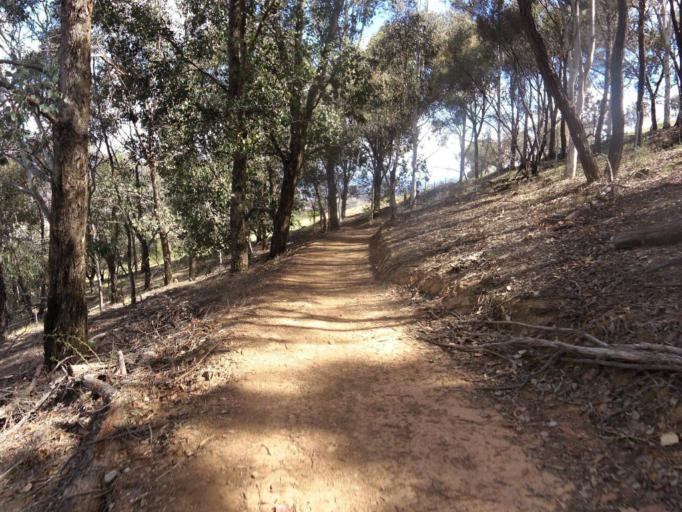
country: AU
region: Australian Capital Territory
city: Belconnen
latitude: -35.1453
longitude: 149.0922
